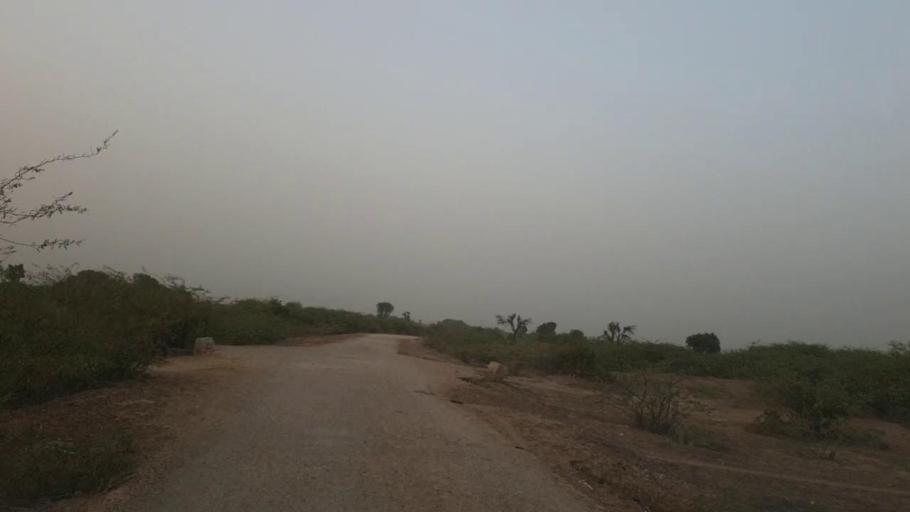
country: PK
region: Sindh
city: Kunri
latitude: 25.1270
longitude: 69.5587
